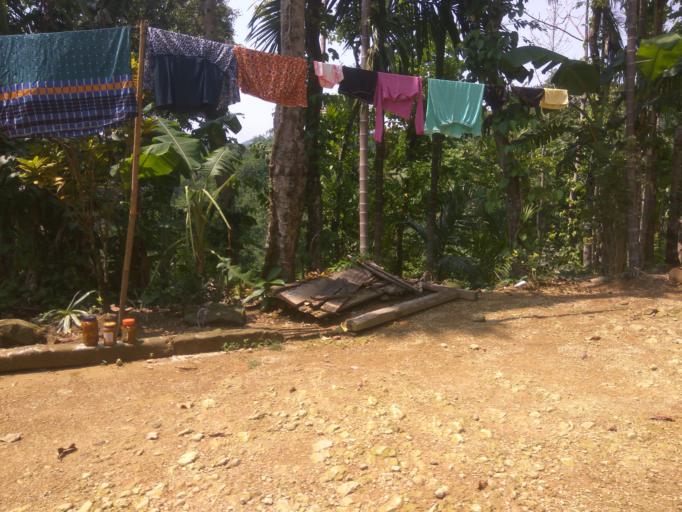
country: IN
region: Assam
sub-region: Karimganj
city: Karimganj
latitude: 25.0269
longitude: 92.4190
